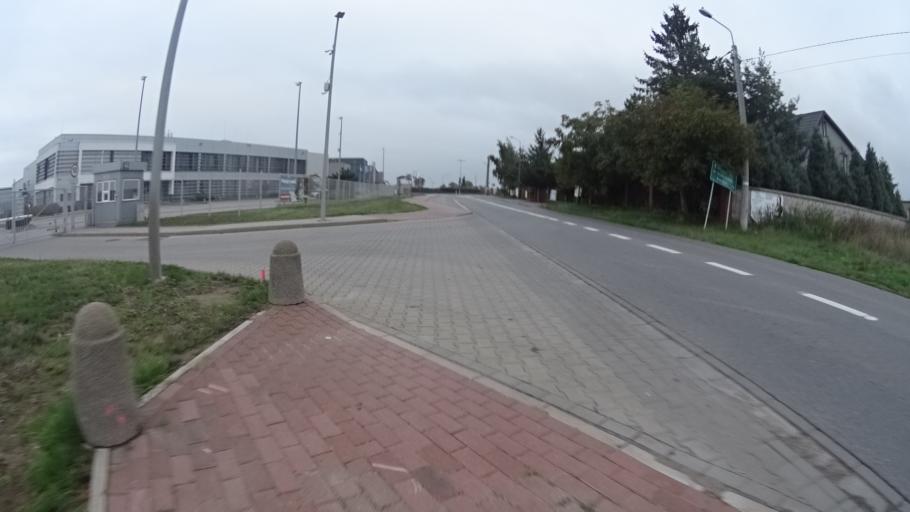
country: PL
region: Masovian Voivodeship
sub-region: Powiat warszawski zachodni
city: Babice
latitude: 52.2305
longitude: 20.8322
